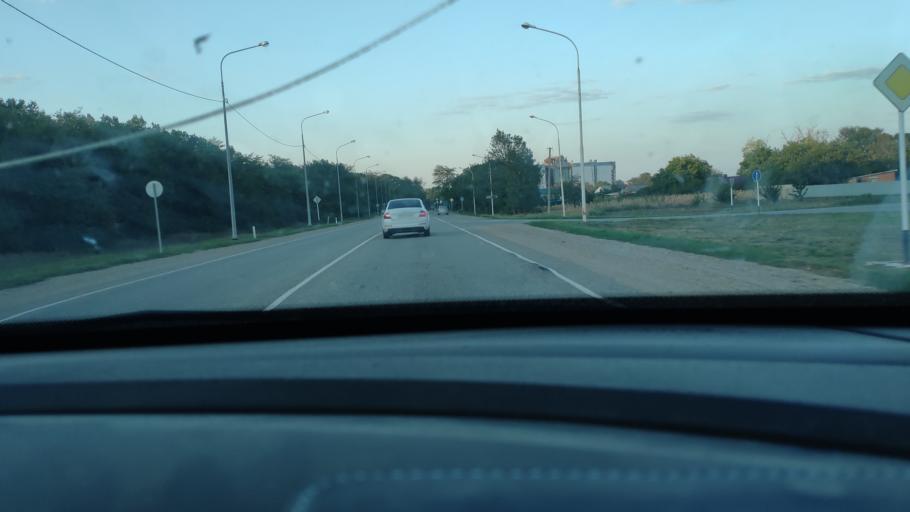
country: RU
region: Krasnodarskiy
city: Novominskaya
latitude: 46.3206
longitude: 38.9327
